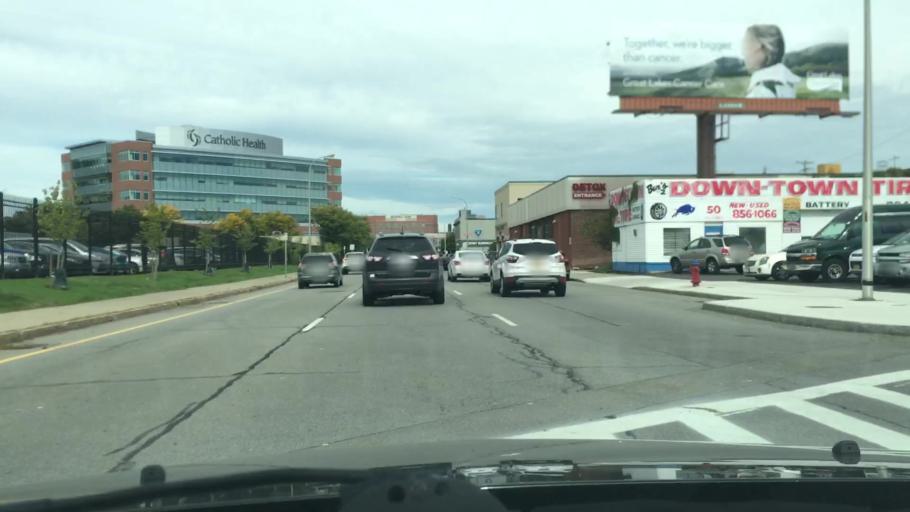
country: US
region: New York
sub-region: Erie County
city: Buffalo
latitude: 42.8886
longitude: -78.8683
